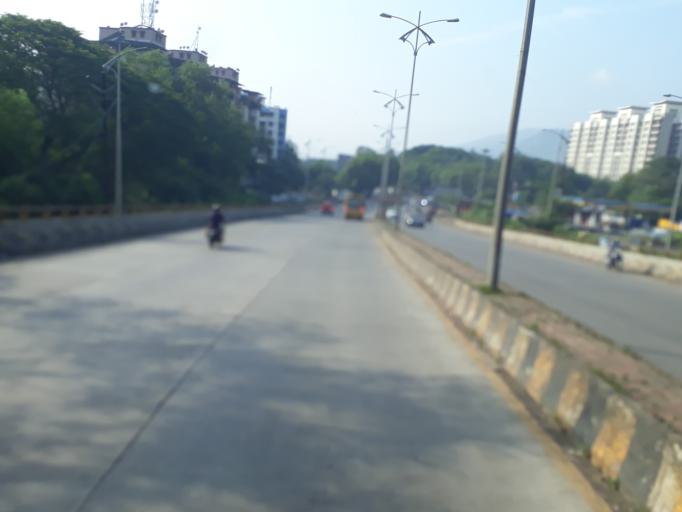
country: IN
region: Maharashtra
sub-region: Raigarh
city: Panvel
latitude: 18.9816
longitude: 73.1161
